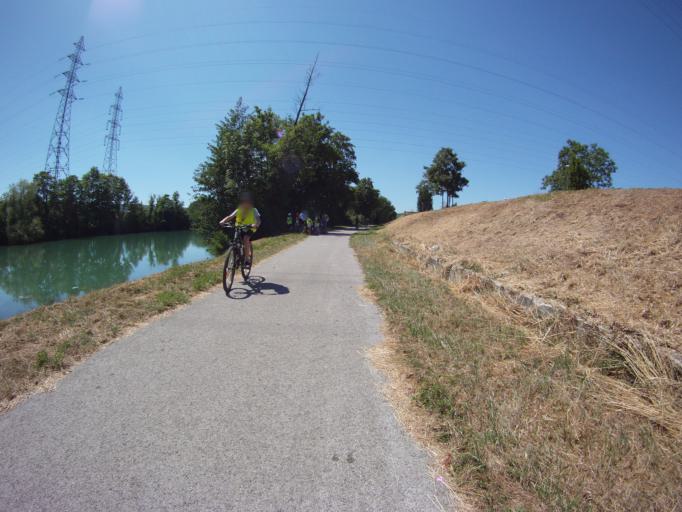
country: FR
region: Champagne-Ardenne
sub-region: Departement de la Marne
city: Damery
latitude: 49.0726
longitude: 3.8697
